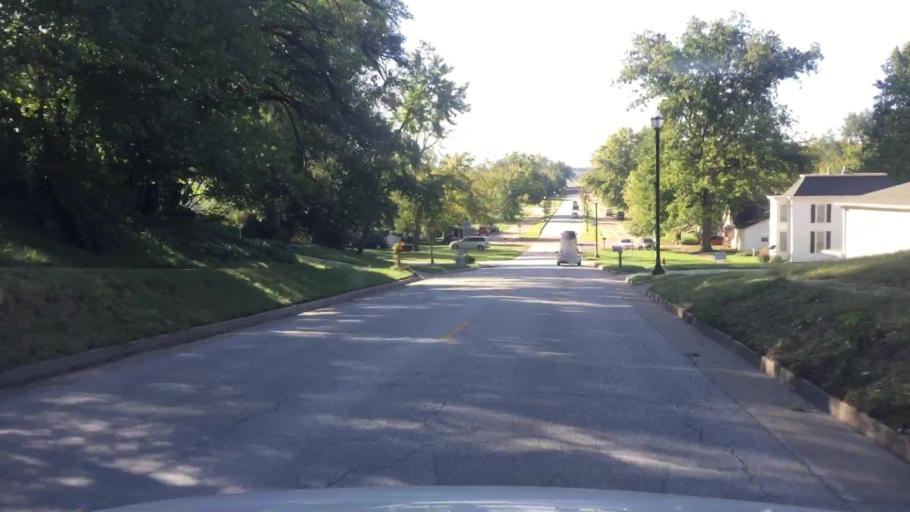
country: US
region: Missouri
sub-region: Howard County
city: New Franklin
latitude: 39.0158
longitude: -92.7374
